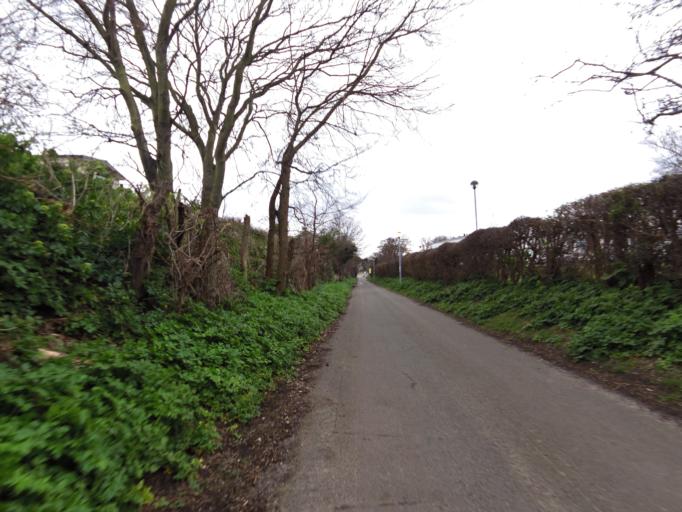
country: GB
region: England
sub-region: Norfolk
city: Hopton on Sea
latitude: 52.5432
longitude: 1.7324
